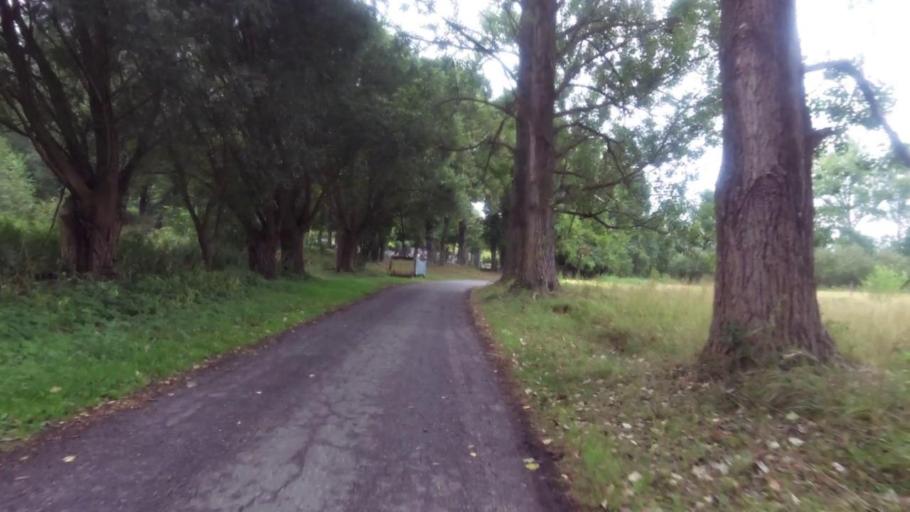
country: PL
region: West Pomeranian Voivodeship
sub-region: Powiat mysliborski
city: Boleszkowice
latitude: 52.6763
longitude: 14.6169
